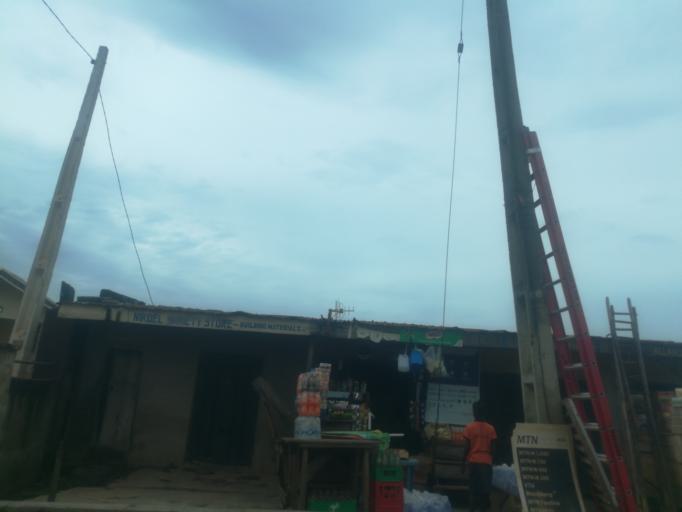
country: NG
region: Oyo
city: Egbeda
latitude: 7.3802
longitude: 3.9942
